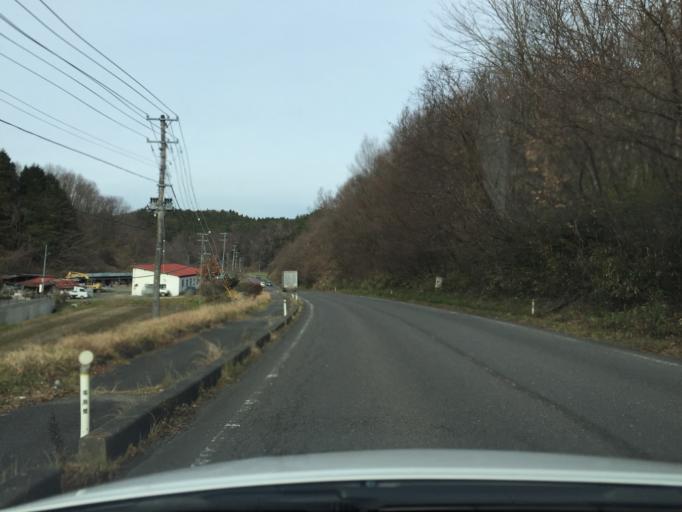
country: JP
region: Fukushima
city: Funehikimachi-funehiki
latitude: 37.2553
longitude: 140.6383
